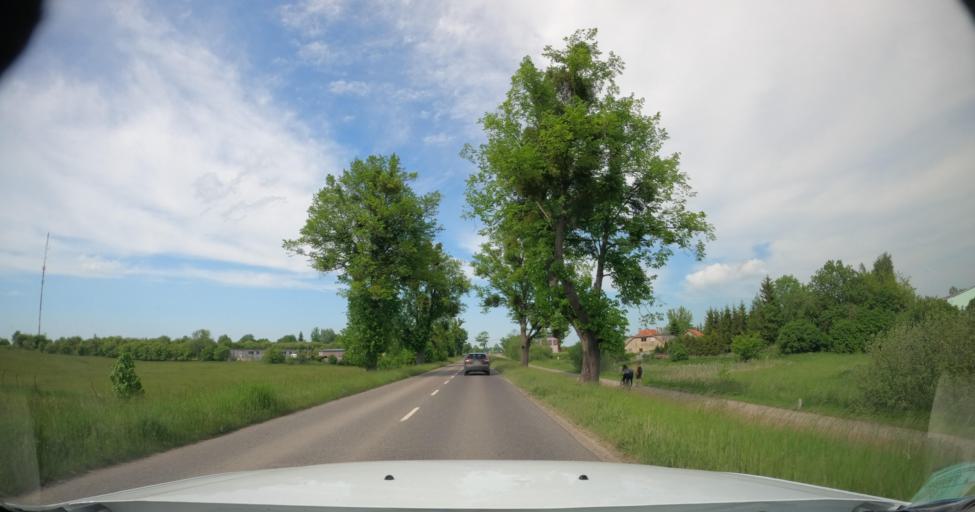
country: PL
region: Warmian-Masurian Voivodeship
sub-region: Powiat lidzbarski
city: Lidzbark Warminski
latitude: 54.1379
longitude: 20.5667
